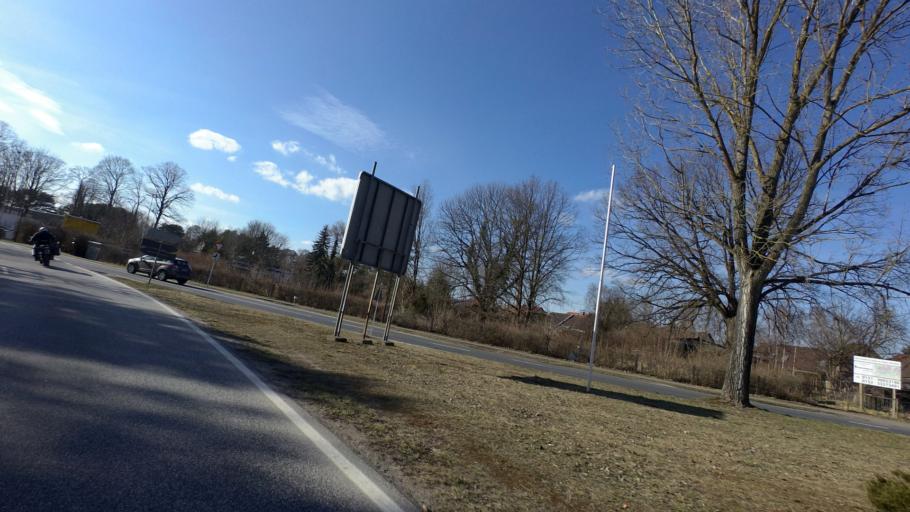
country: DE
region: Brandenburg
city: Oranienburg
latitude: 52.7679
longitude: 13.3242
